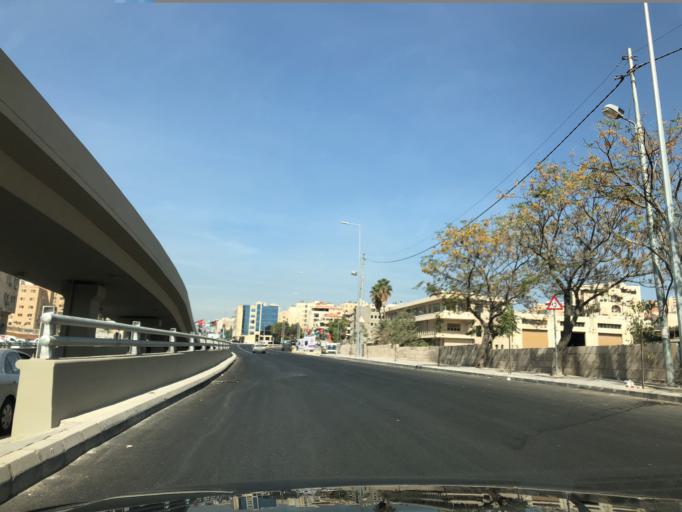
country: JO
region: Amman
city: Al Jubayhah
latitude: 31.9914
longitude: 35.8920
